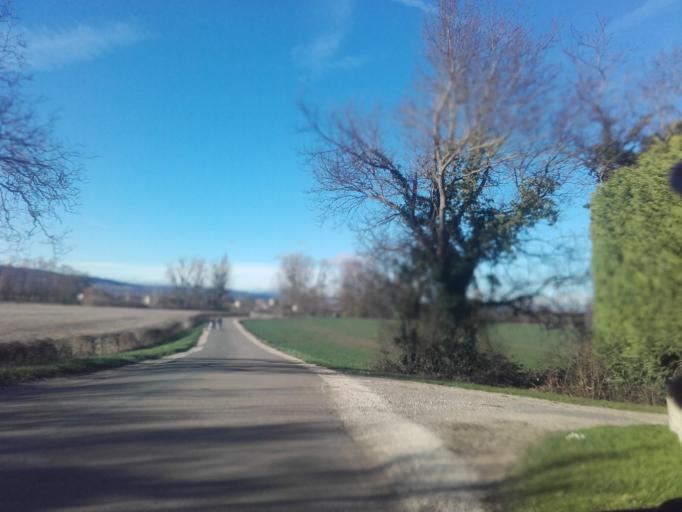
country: FR
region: Bourgogne
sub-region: Departement de la Cote-d'Or
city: Corpeau
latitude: 46.9214
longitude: 4.7879
